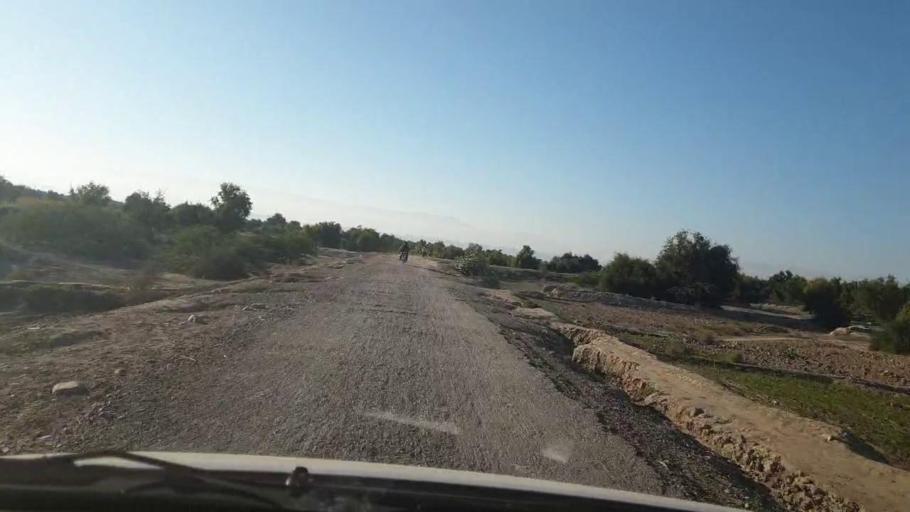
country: PK
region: Sindh
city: Johi
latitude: 26.7601
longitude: 67.4696
